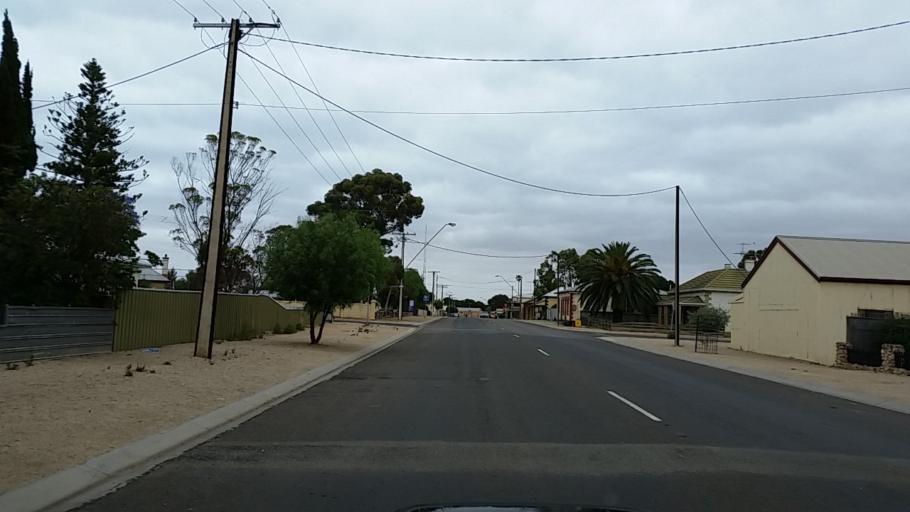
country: AU
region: South Australia
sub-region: Wakefield
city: Balaklava
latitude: -34.1852
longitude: 138.1508
